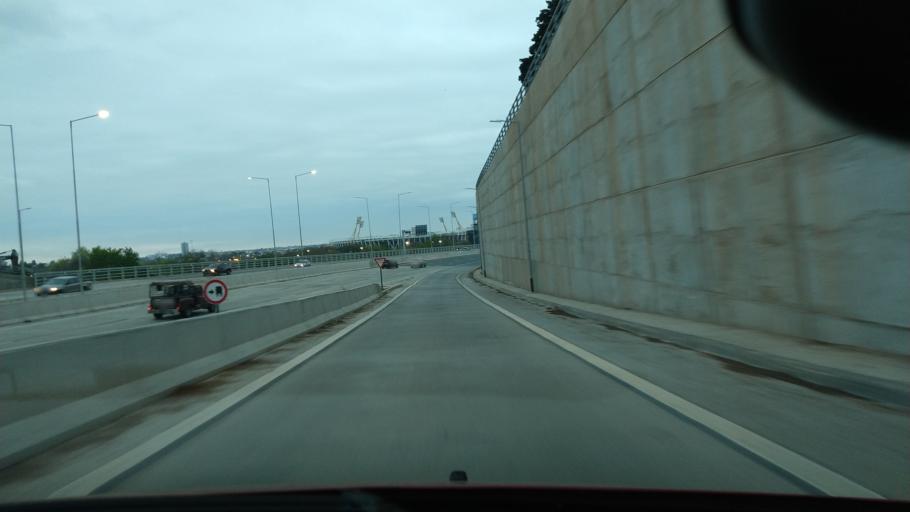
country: AR
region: Cordoba
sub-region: Departamento de Capital
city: Cordoba
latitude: -31.3604
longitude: -64.2416
